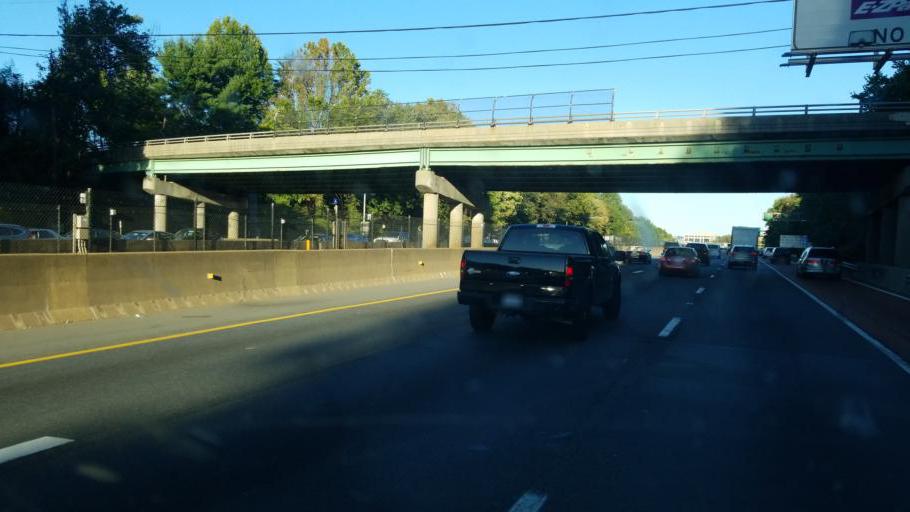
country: US
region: Virginia
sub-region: Fairfax County
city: Merrifield
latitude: 38.8794
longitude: -77.2474
